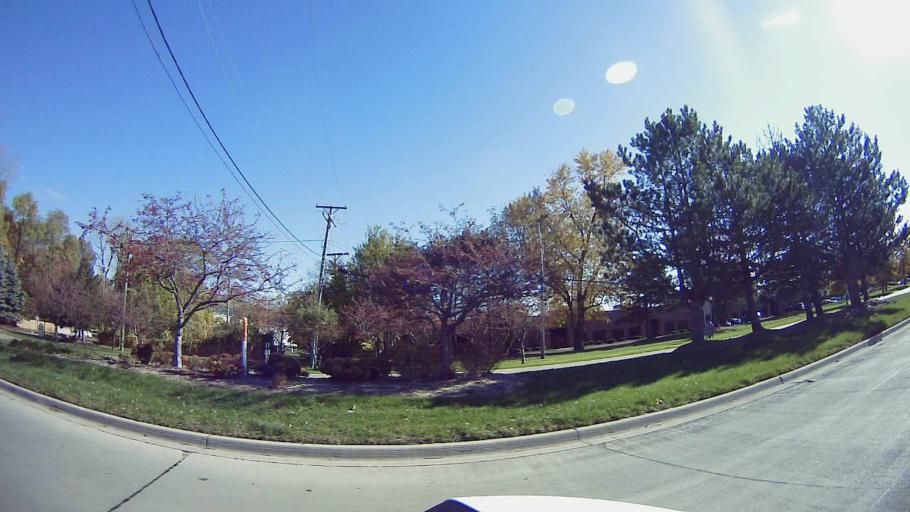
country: US
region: Michigan
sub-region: Oakland County
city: Southfield
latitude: 42.4483
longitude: -83.2597
